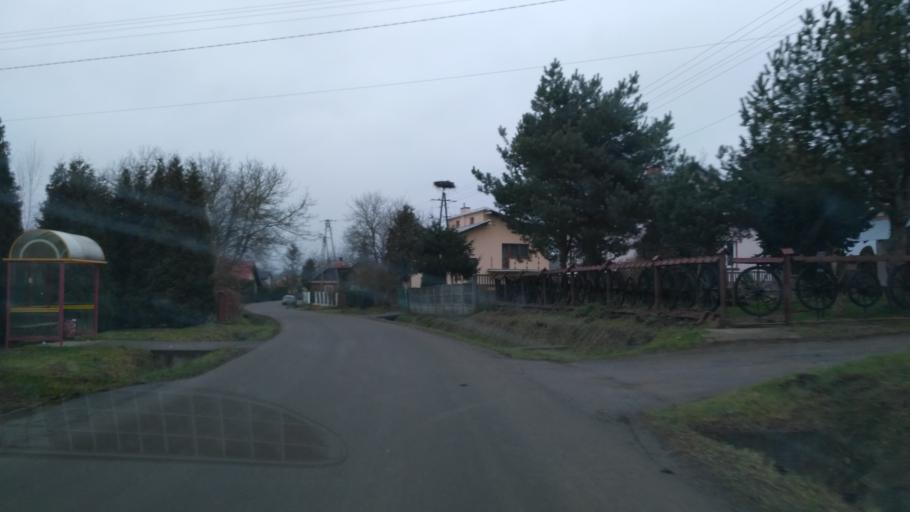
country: PL
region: Subcarpathian Voivodeship
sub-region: Powiat jaroslawski
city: Pruchnik
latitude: 49.9289
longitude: 22.5359
